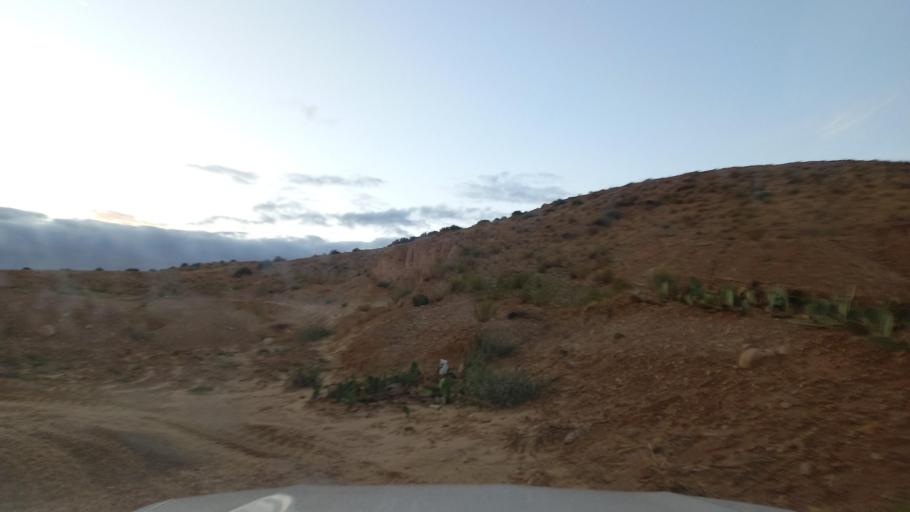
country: TN
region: Al Qasrayn
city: Kasserine
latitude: 35.2563
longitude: 8.9334
